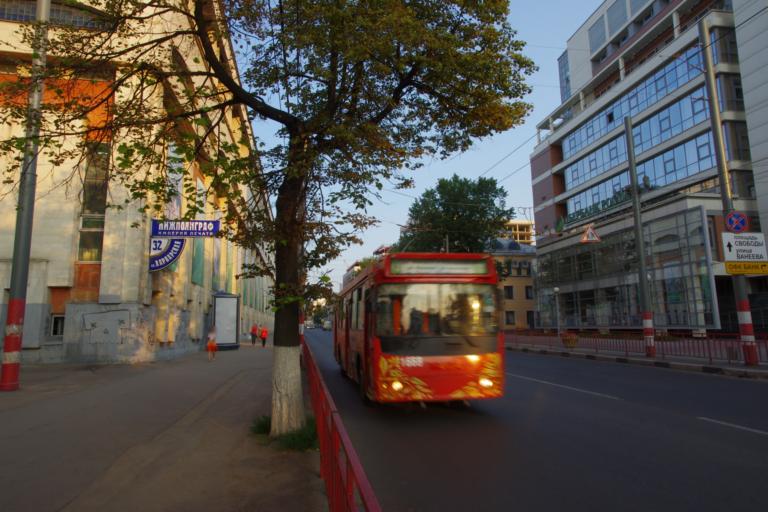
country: RU
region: Nizjnij Novgorod
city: Nizhniy Novgorod
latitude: 56.3225
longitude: 44.0113
